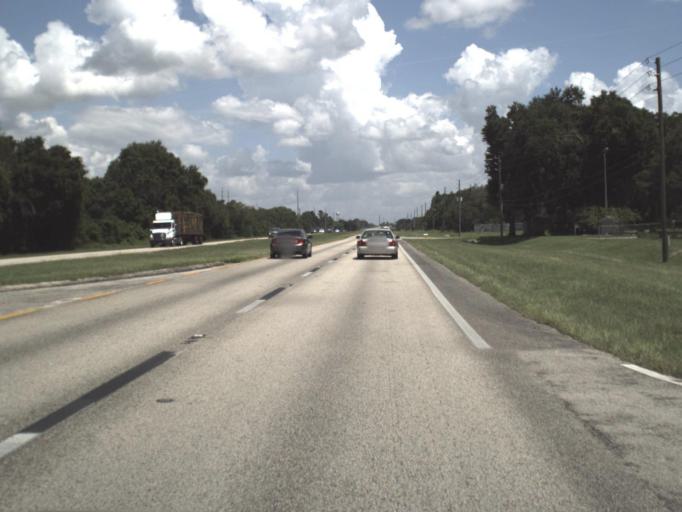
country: US
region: Florida
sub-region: Polk County
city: Eagle Lake
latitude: 27.9608
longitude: -81.7778
